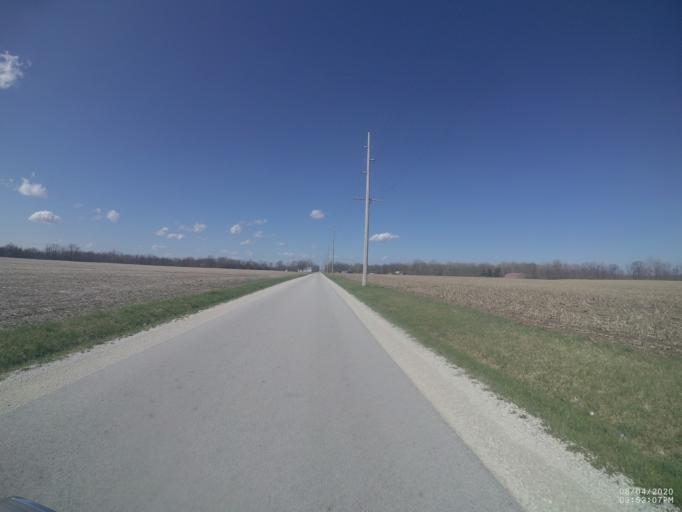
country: US
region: Ohio
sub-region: Sandusky County
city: Ballville
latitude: 41.2634
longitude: -83.1879
